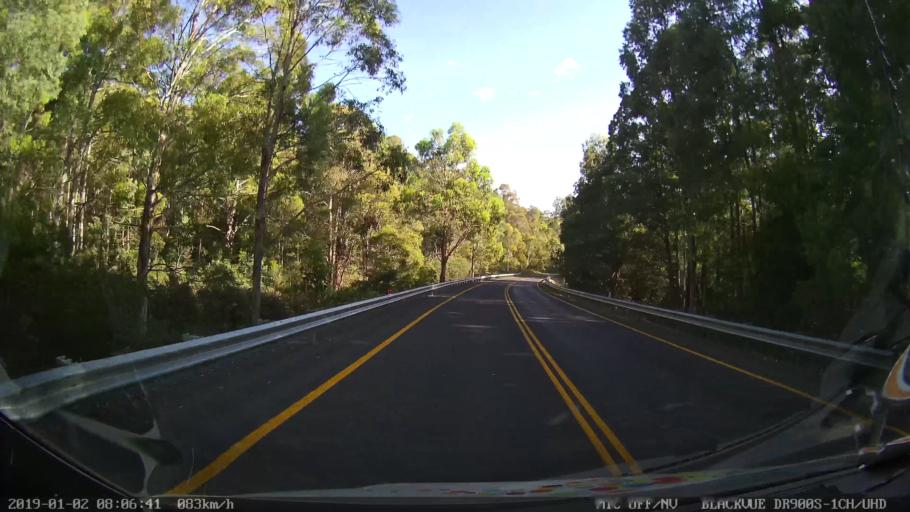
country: AU
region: New South Wales
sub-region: Tumut Shire
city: Tumut
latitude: -35.6370
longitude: 148.3869
